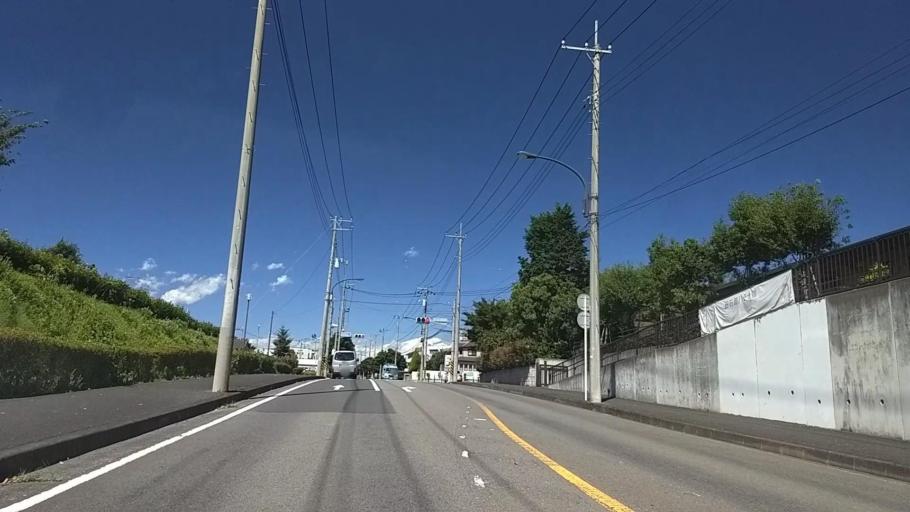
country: JP
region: Kanagawa
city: Zama
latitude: 35.5288
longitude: 139.3558
